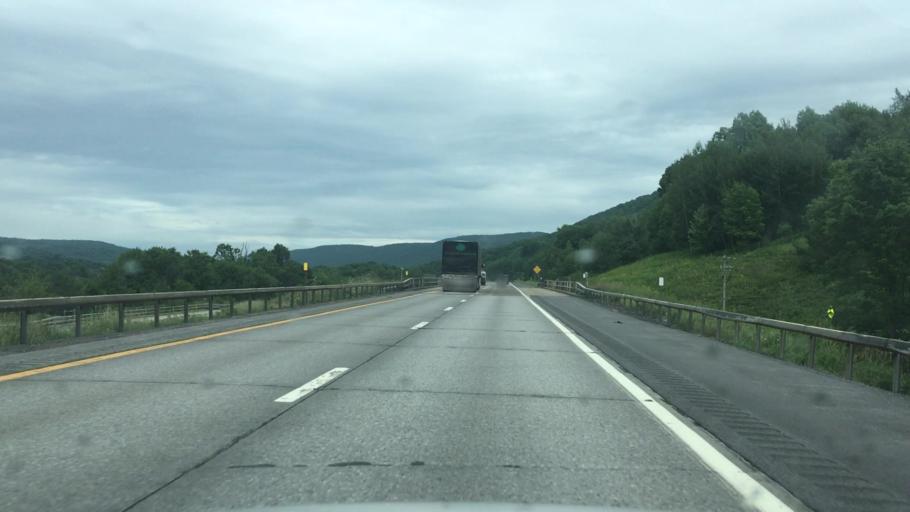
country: US
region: New York
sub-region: Otsego County
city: Worcester
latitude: 42.5860
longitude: -74.7511
